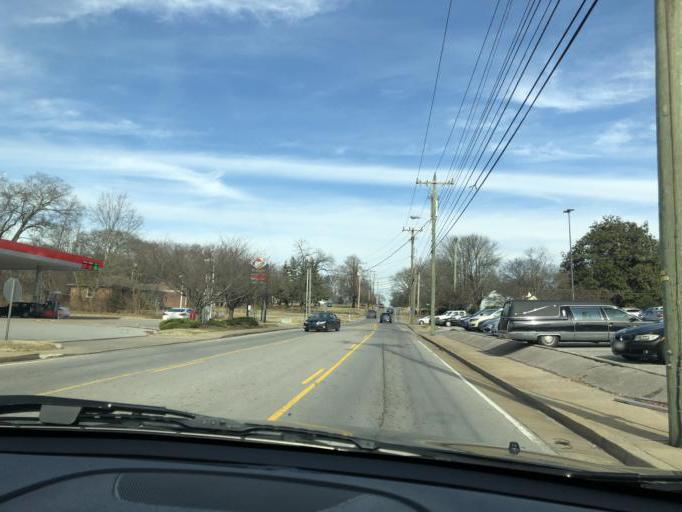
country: US
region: Tennessee
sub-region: Davidson County
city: Lakewood
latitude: 36.1707
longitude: -86.6796
